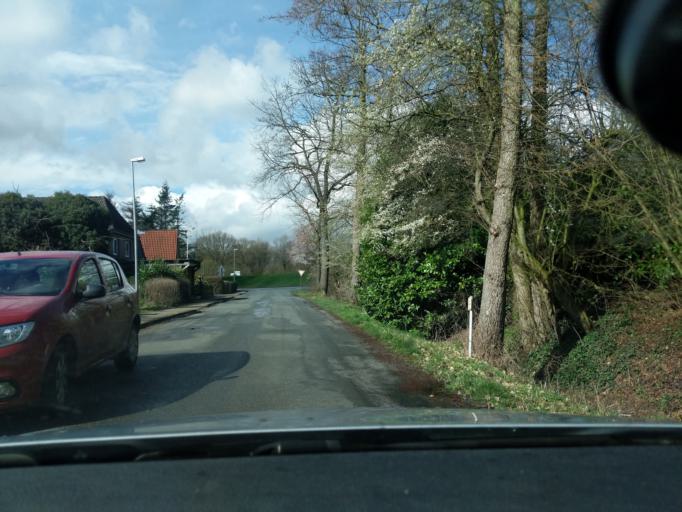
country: DE
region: Lower Saxony
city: Stade
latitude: 53.6130
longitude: 9.5068
